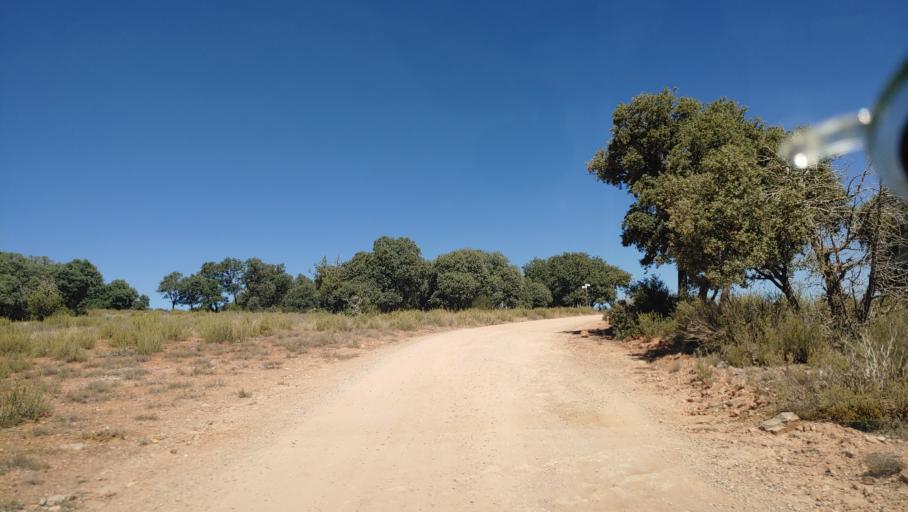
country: ES
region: Castille-La Mancha
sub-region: Provincia de Albacete
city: Ossa de Montiel
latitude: 38.9191
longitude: -2.7992
